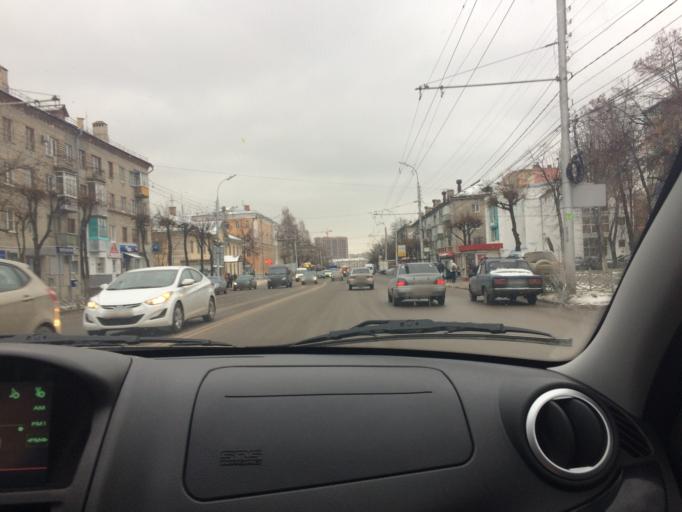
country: RU
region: Rjazan
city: Ryazan'
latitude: 54.6202
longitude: 39.7245
